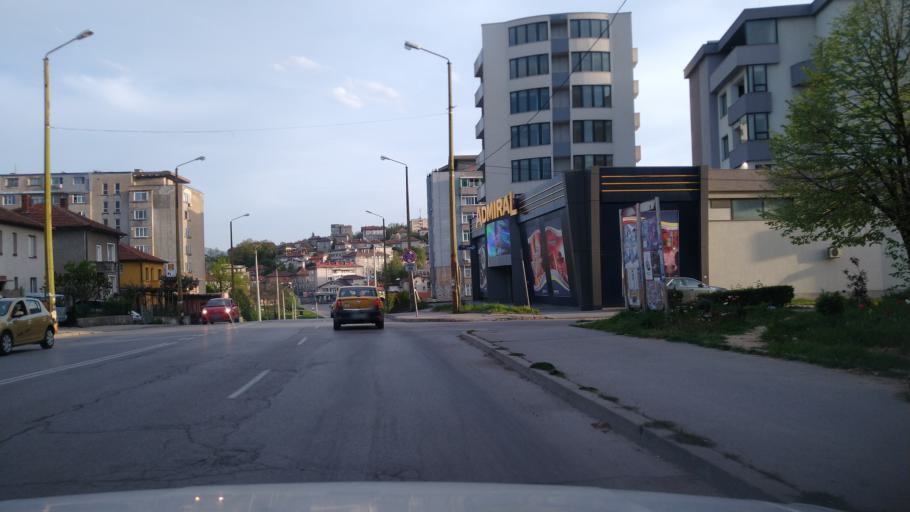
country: BG
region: Gabrovo
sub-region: Obshtina Gabrovo
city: Gabrovo
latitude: 42.8822
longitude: 25.3127
